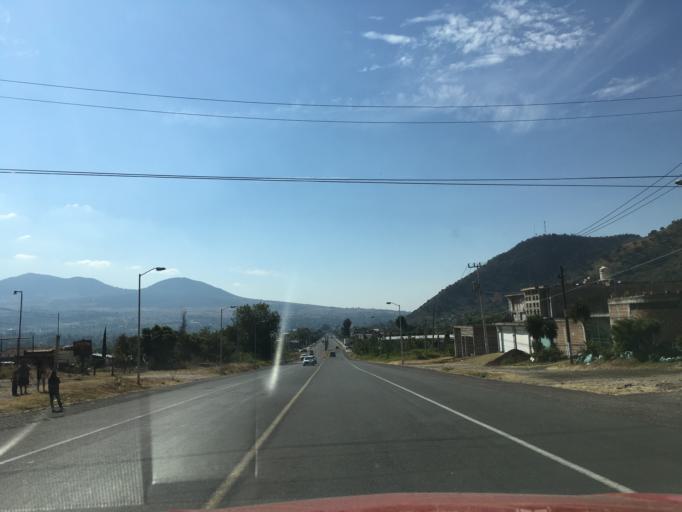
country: MX
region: Michoacan
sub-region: Tuxpan
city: Santa Ana
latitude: 19.5860
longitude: -100.4663
